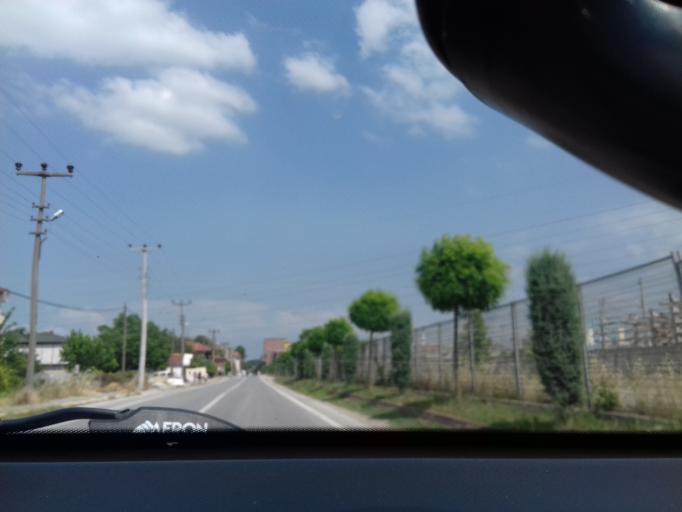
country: TR
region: Sakarya
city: Adapazari
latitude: 40.7136
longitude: 30.3510
